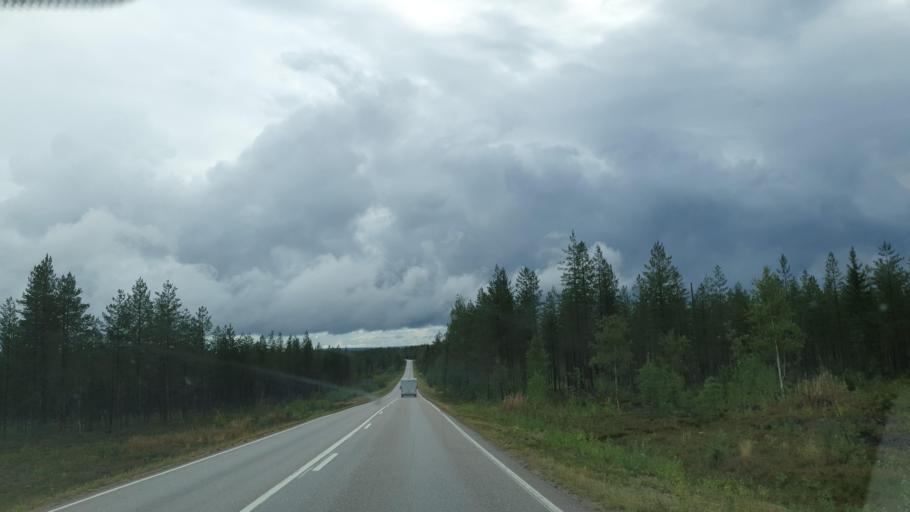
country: FI
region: Kainuu
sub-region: Kehys-Kainuu
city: Puolanka
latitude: 64.9449
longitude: 27.6016
